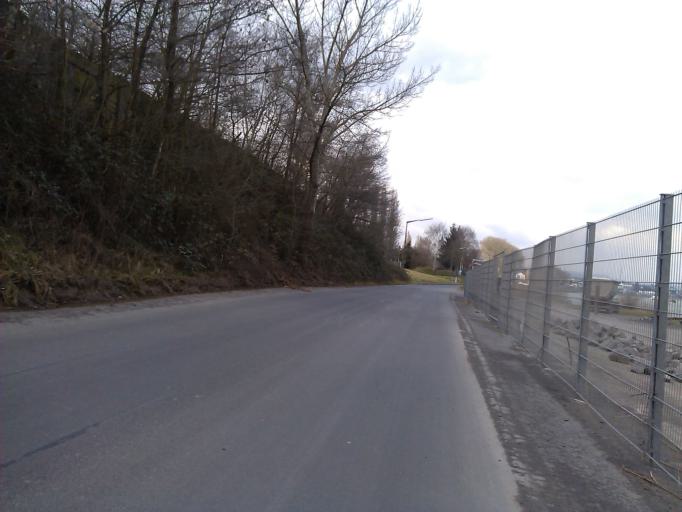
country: DE
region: Rheinland-Pfalz
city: Kettig
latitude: 50.4116
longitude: 7.4715
